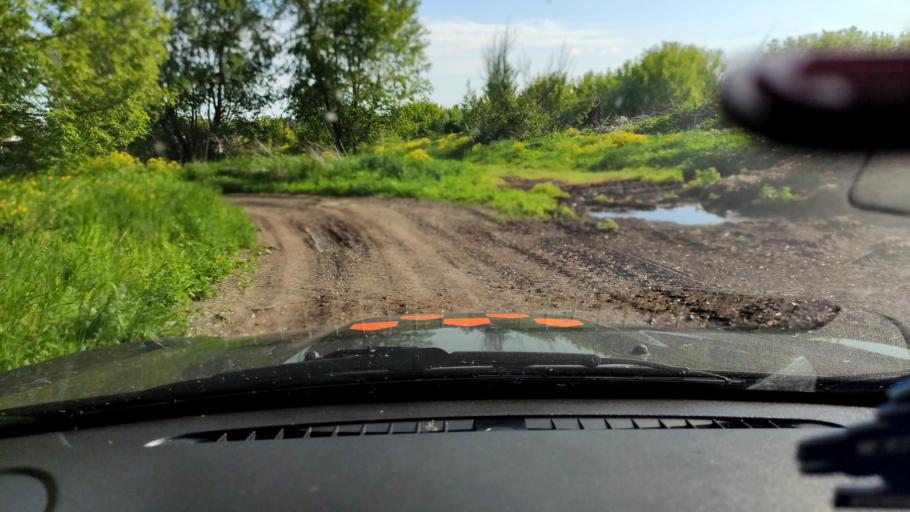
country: RU
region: Voronezj
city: Uryv-Pokrovka
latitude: 51.1203
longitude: 39.1781
